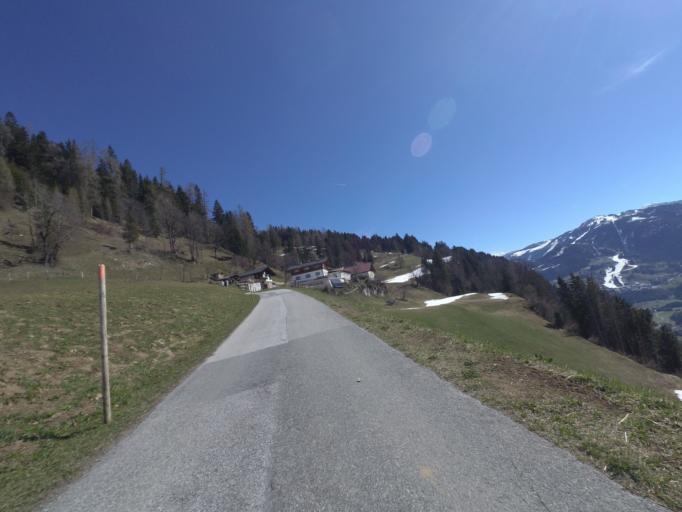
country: AT
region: Salzburg
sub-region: Politischer Bezirk Sankt Johann im Pongau
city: Sankt Veit im Pongau
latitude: 47.3393
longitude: 13.1525
